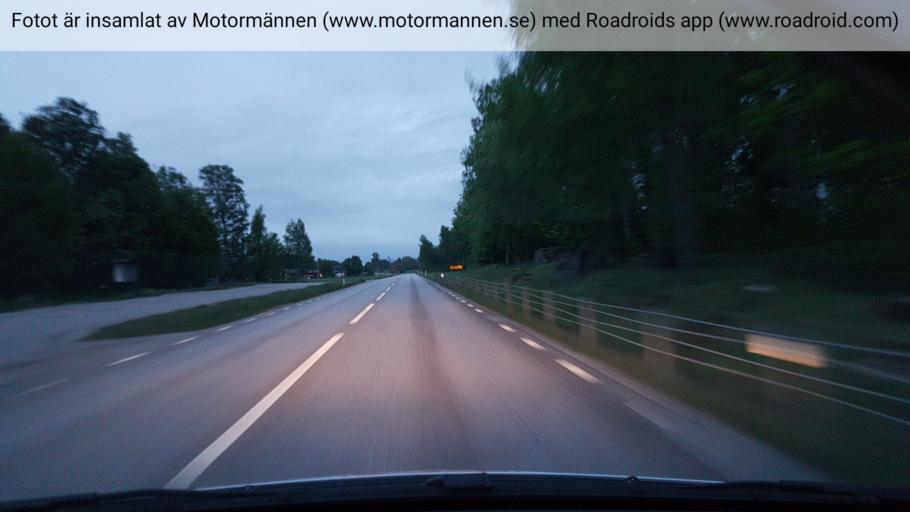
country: SE
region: Vaestmanland
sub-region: Sala Kommun
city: Sala
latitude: 59.8365
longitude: 16.6869
